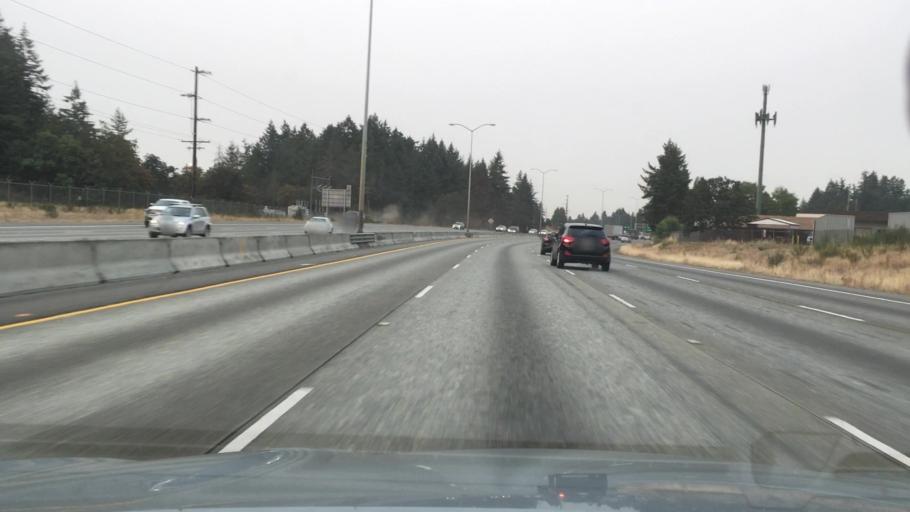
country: US
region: Washington
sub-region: Pierce County
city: McChord Air Force Base
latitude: 47.1412
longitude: -122.5157
